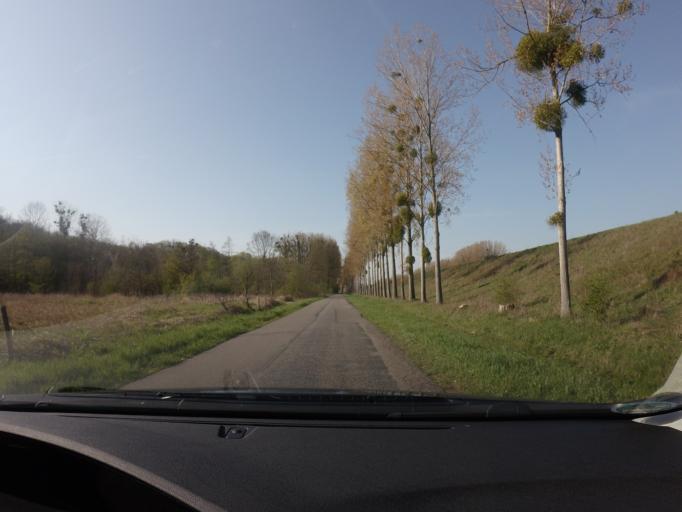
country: NL
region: Limburg
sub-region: Gemeente Stein
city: Elsloo
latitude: 50.9384
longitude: 5.7506
